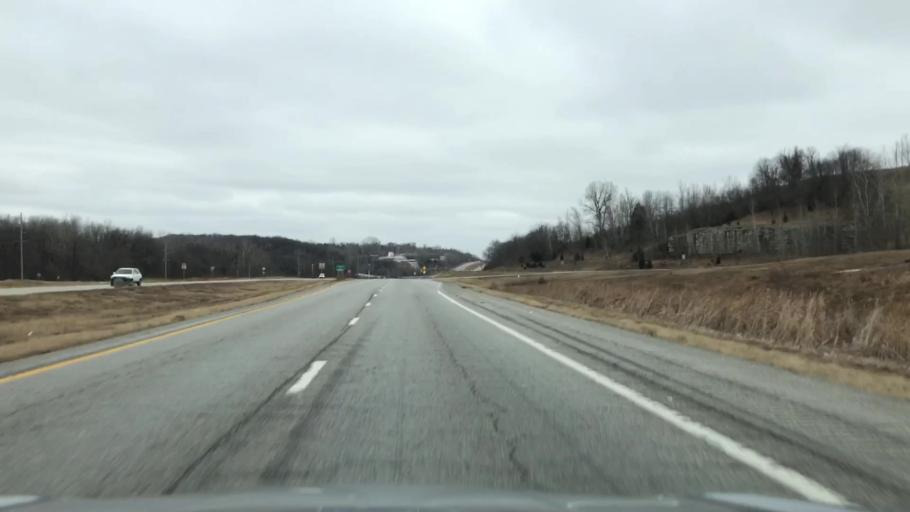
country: US
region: Missouri
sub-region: Jackson County
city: East Independence
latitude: 39.1389
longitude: -94.3871
